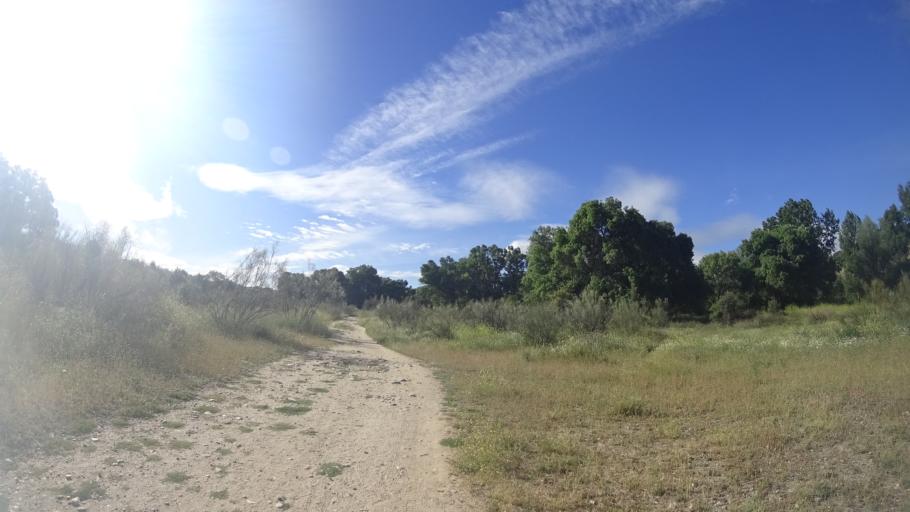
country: ES
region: Madrid
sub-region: Provincia de Madrid
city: Villanueva del Pardillo
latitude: 40.5147
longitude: -3.9412
